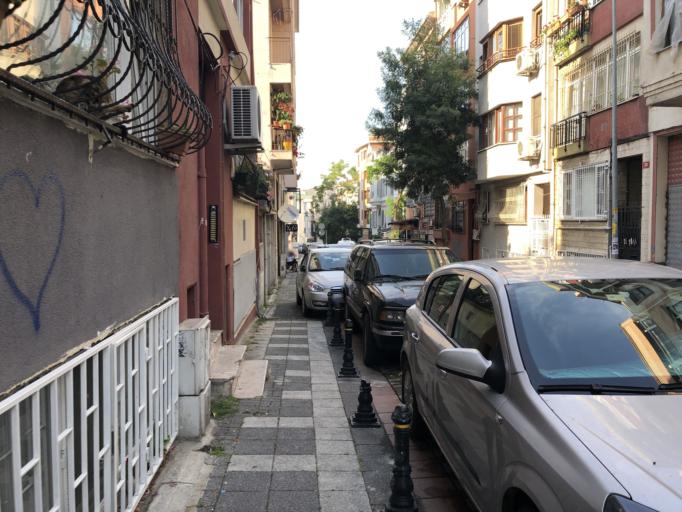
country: TR
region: Istanbul
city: UEskuedar
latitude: 40.9837
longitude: 29.0289
